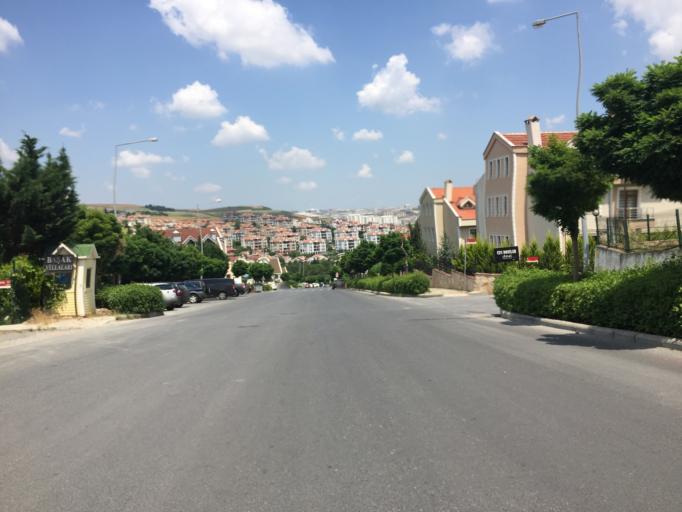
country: TR
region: Istanbul
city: Esenyurt
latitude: 41.0793
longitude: 28.6676
